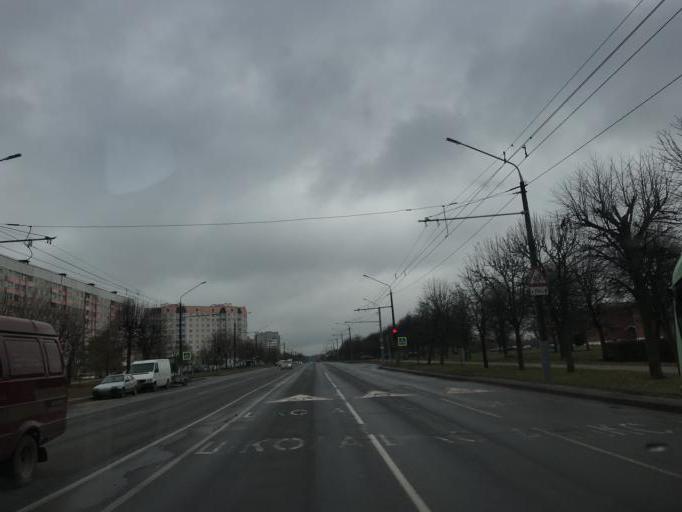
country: BY
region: Mogilev
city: Mahilyow
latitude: 53.8693
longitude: 30.3257
